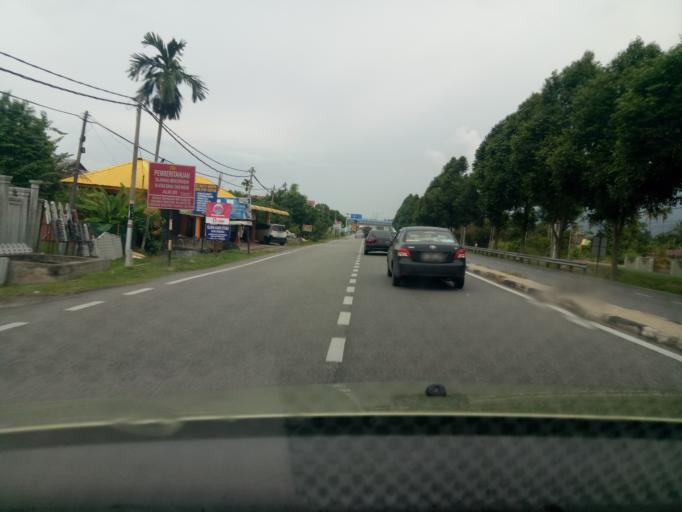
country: MY
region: Kedah
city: Gurun
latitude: 5.8627
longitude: 100.4555
